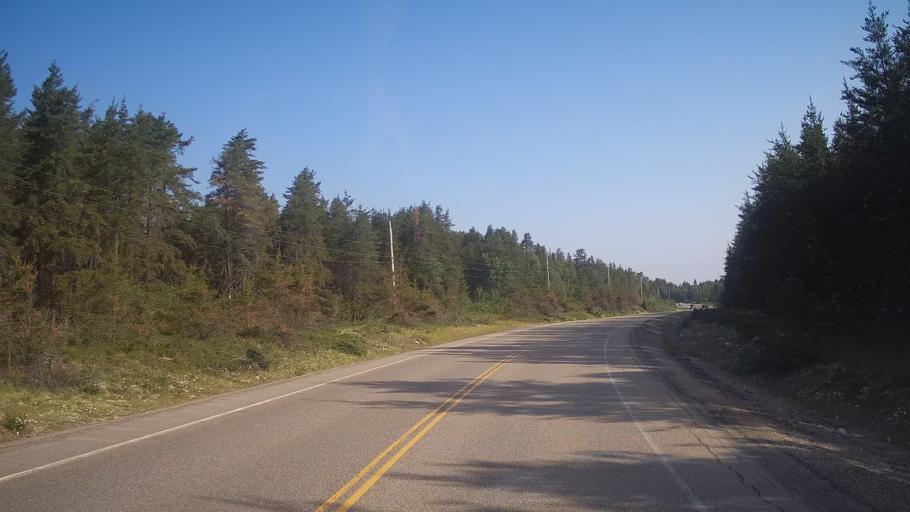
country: CA
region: Ontario
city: Rayside-Balfour
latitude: 46.7083
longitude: -81.5615
